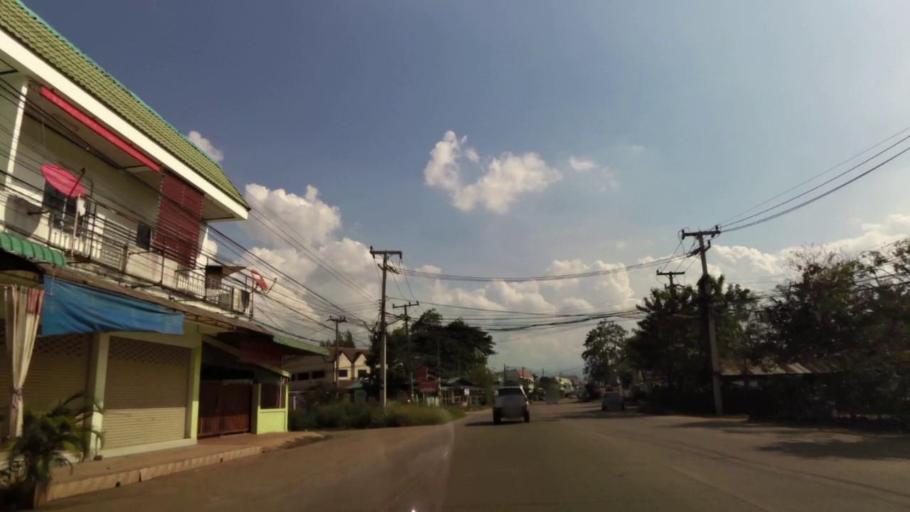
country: TH
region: Phrae
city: Phrae
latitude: 18.1243
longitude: 100.1521
